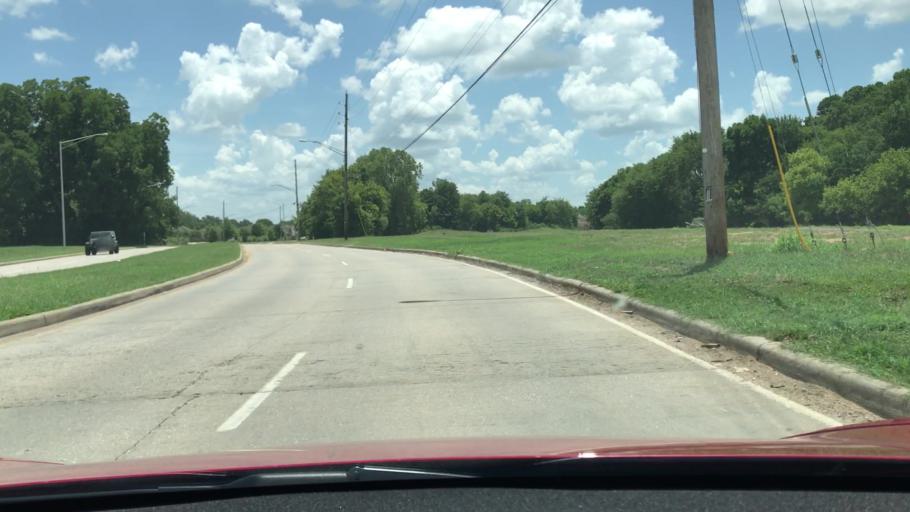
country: US
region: Louisiana
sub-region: Bossier Parish
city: Bossier City
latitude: 32.4360
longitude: -93.7285
